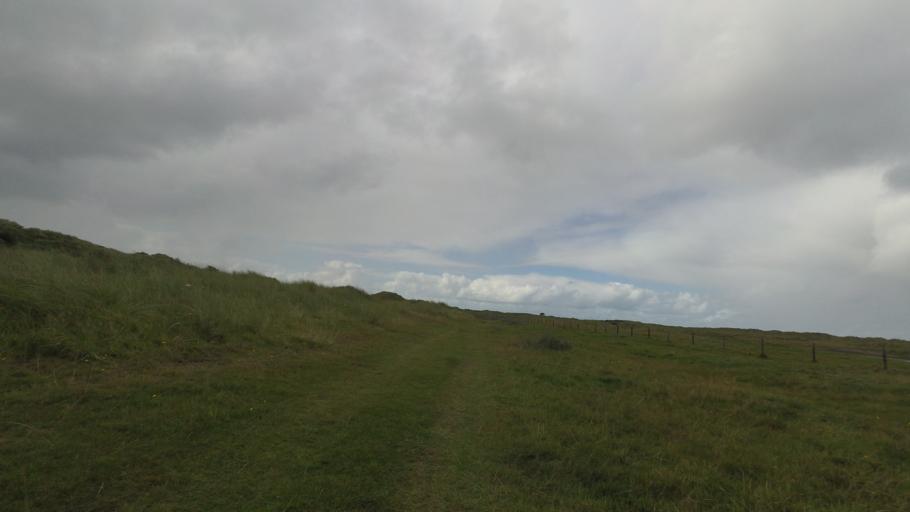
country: NL
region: Friesland
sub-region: Gemeente Ameland
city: Nes
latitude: 53.4529
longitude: 5.8444
